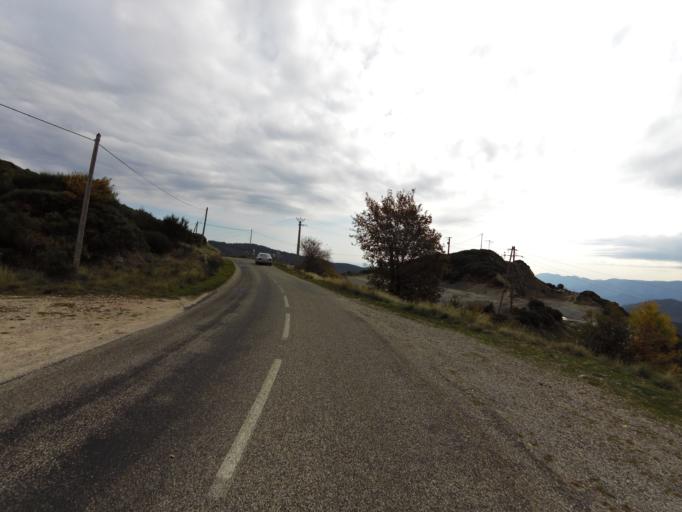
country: FR
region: Rhone-Alpes
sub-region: Departement de l'Ardeche
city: Les Vans
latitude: 44.5075
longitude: 4.0445
